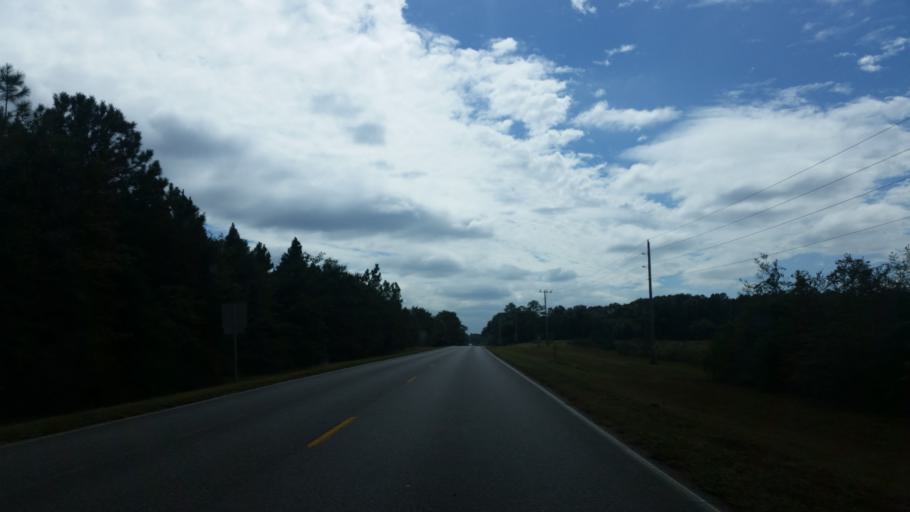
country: US
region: Florida
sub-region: Santa Rosa County
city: Point Baker
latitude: 30.7727
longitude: -86.9410
